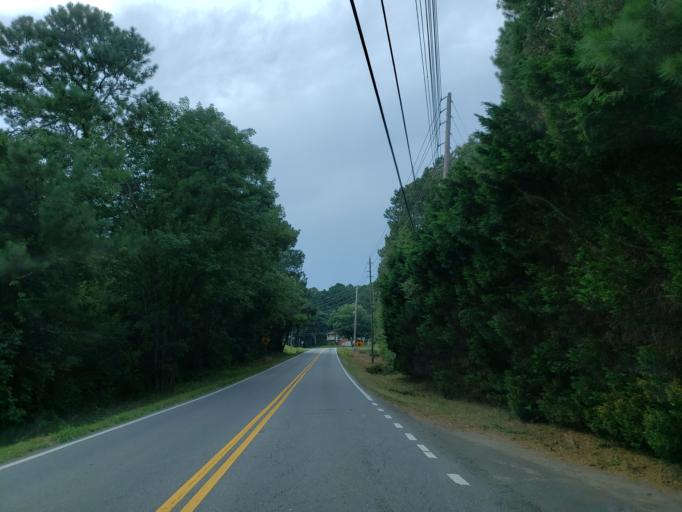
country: US
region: Georgia
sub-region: Cherokee County
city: Holly Springs
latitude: 34.1249
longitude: -84.4086
